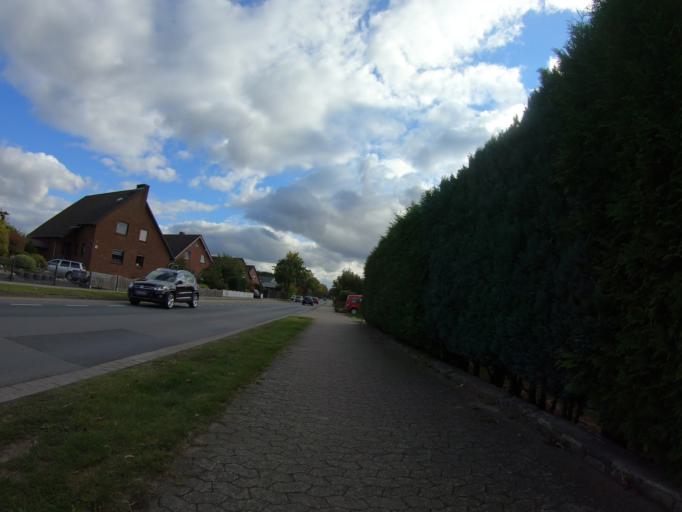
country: DE
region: Lower Saxony
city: Isenbuttel
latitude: 52.4301
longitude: 10.5842
